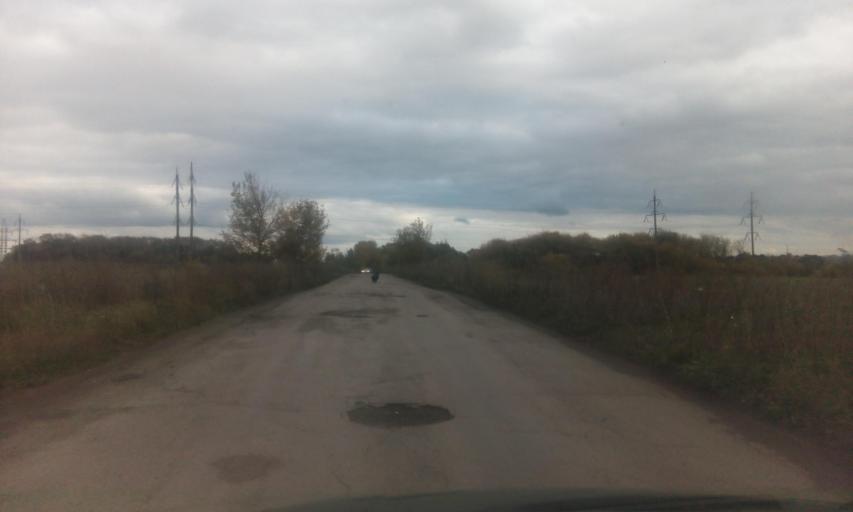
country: RU
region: Tula
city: Gritsovskiy
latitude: 54.1283
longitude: 38.1615
